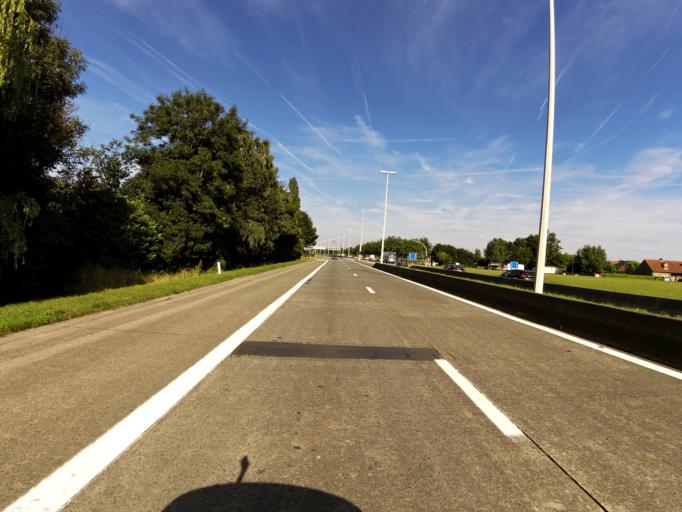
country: BE
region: Flanders
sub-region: Provincie Oost-Vlaanderen
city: Maldegem
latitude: 51.2209
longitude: 3.4292
